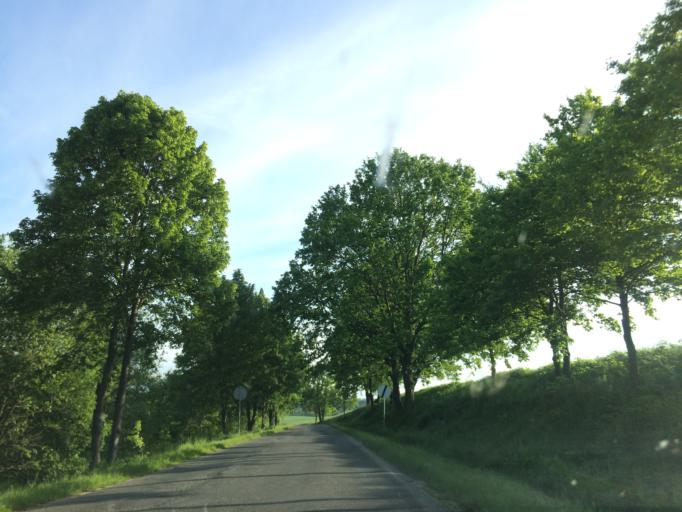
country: PL
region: Lower Silesian Voivodeship
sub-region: Powiat swidnicki
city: Swidnica
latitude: 50.7901
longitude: 16.5013
